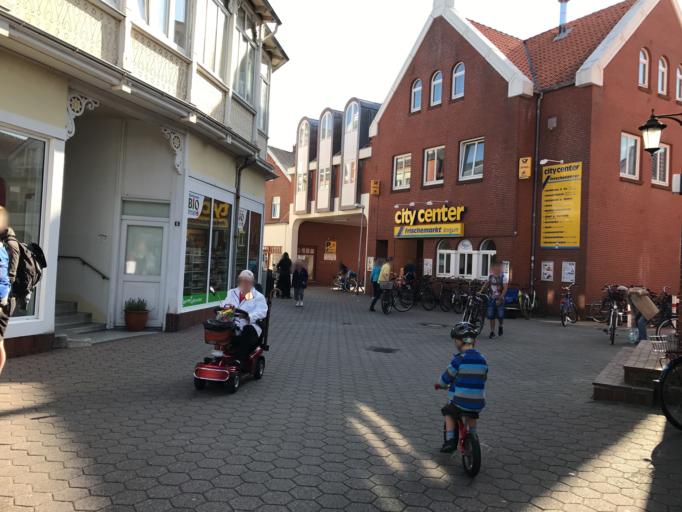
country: DE
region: Lower Saxony
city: Borkum
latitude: 53.5881
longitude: 6.6650
